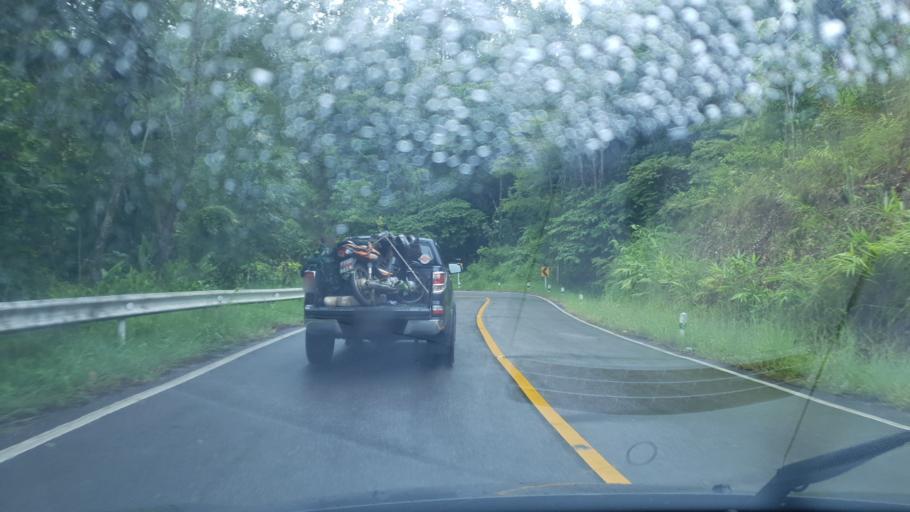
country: TH
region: Mae Hong Son
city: Mae La Noi
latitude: 18.5514
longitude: 97.9351
